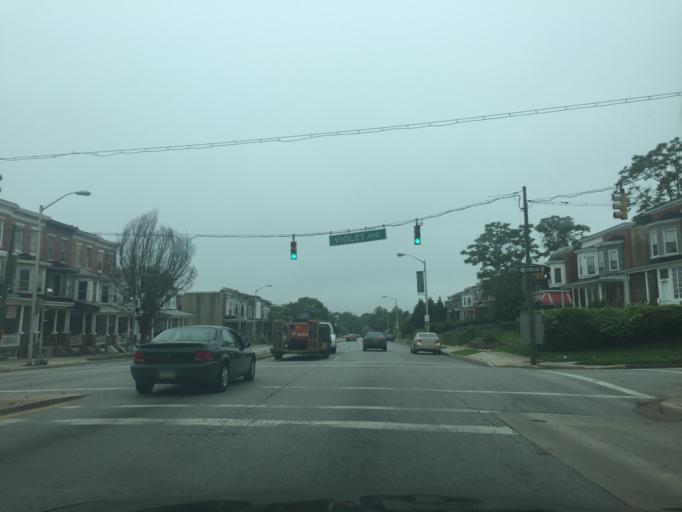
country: US
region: Maryland
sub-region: City of Baltimore
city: Baltimore
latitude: 39.3309
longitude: -76.6600
